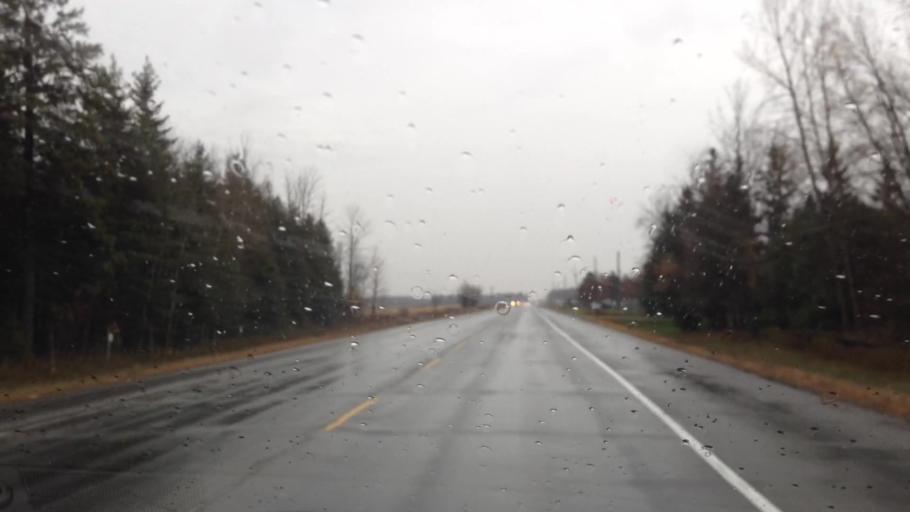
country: CA
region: Ontario
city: Clarence-Rockland
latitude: 45.4301
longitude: -75.4126
